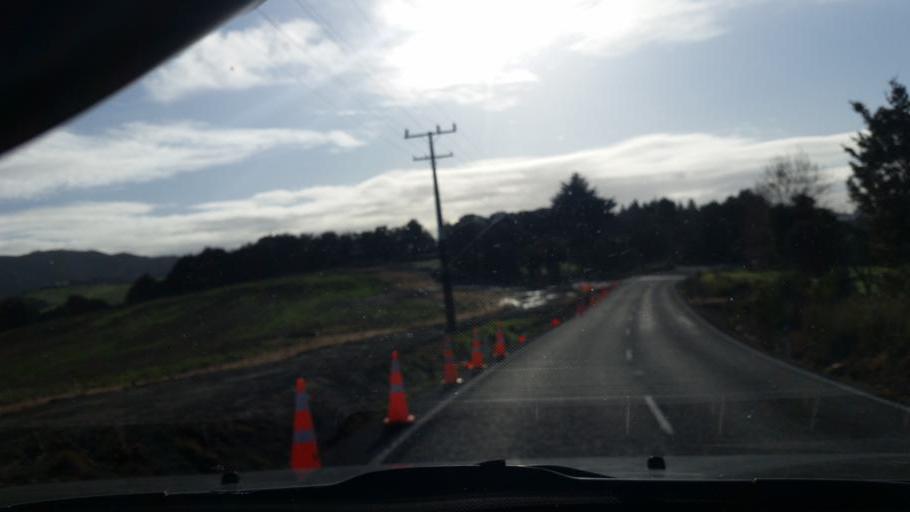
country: NZ
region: Auckland
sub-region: Auckland
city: Wellsford
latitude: -36.0981
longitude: 174.5584
